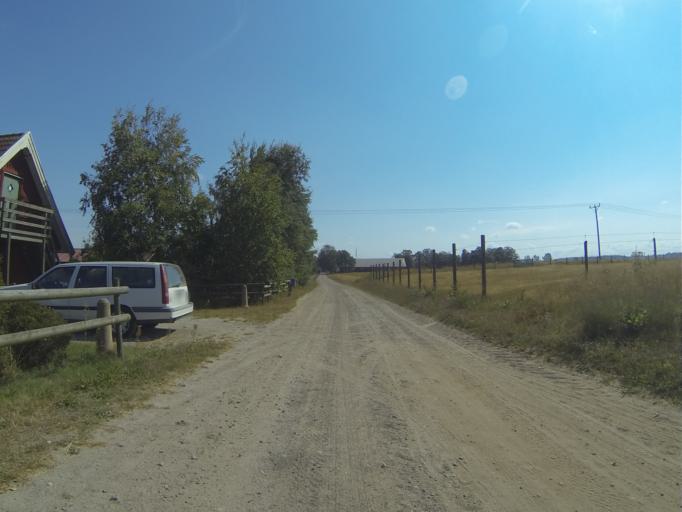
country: SE
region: Skane
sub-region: Eslovs Kommun
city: Eslov
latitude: 55.7366
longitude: 13.3541
